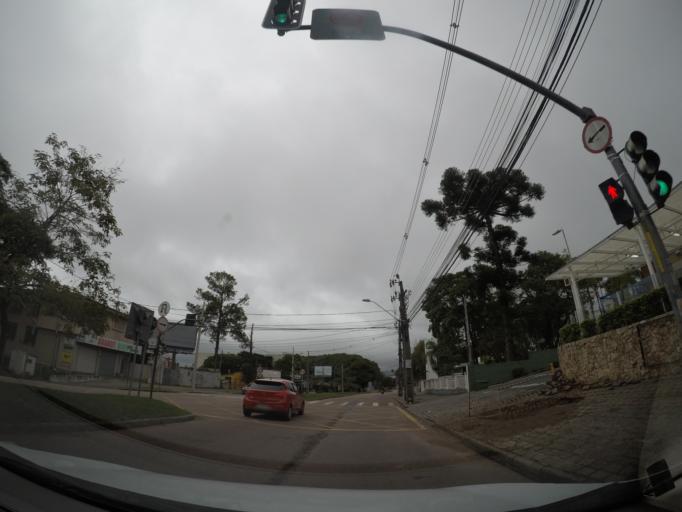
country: BR
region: Parana
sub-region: Curitiba
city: Curitiba
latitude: -25.4493
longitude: -49.2999
